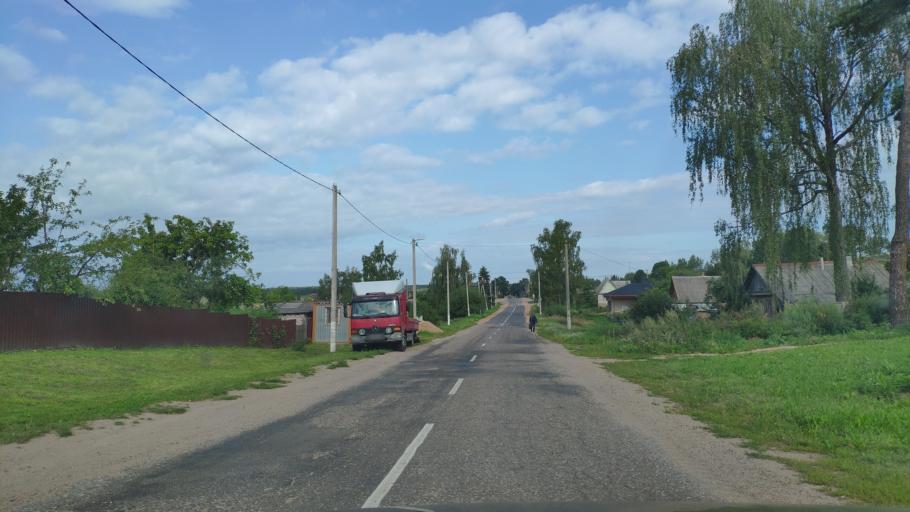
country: BY
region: Minsk
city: Khatsyezhyna
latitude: 53.8876
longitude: 27.2659
